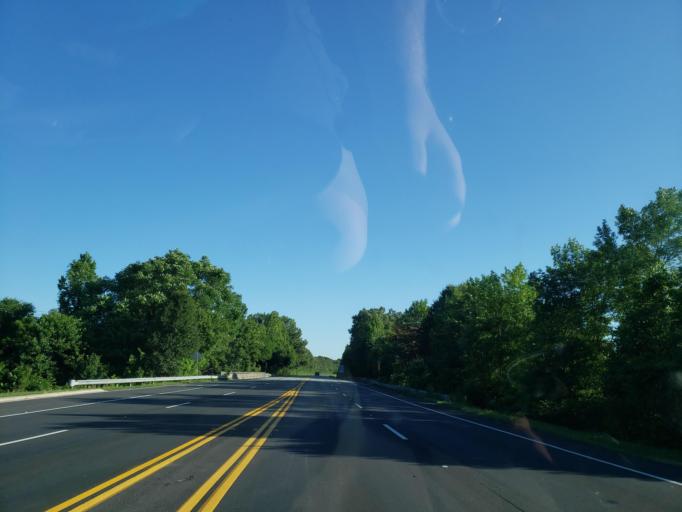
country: US
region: Georgia
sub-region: Floyd County
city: Rome
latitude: 34.2995
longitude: -85.1771
